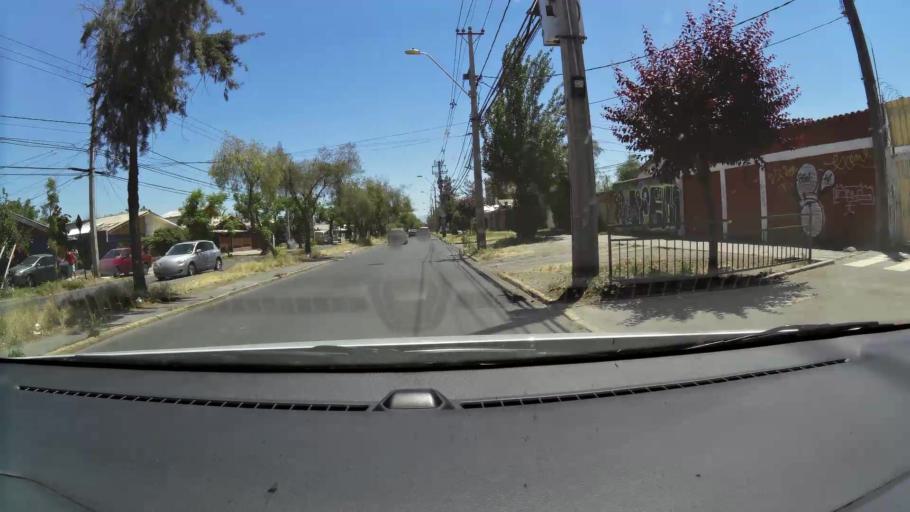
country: CL
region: Santiago Metropolitan
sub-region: Provincia de Maipo
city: San Bernardo
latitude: -33.5781
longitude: -70.6877
